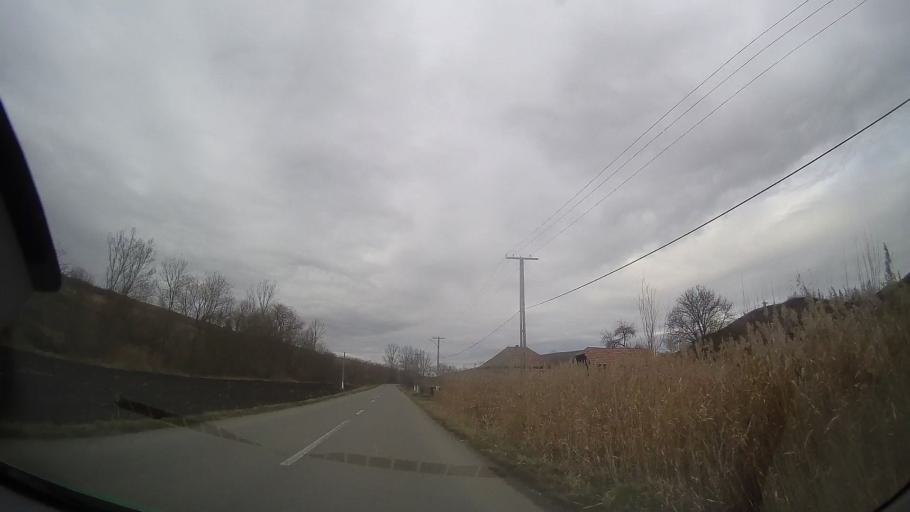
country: RO
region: Mures
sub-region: Comuna Faragau
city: Faragau
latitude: 46.7354
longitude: 24.5433
